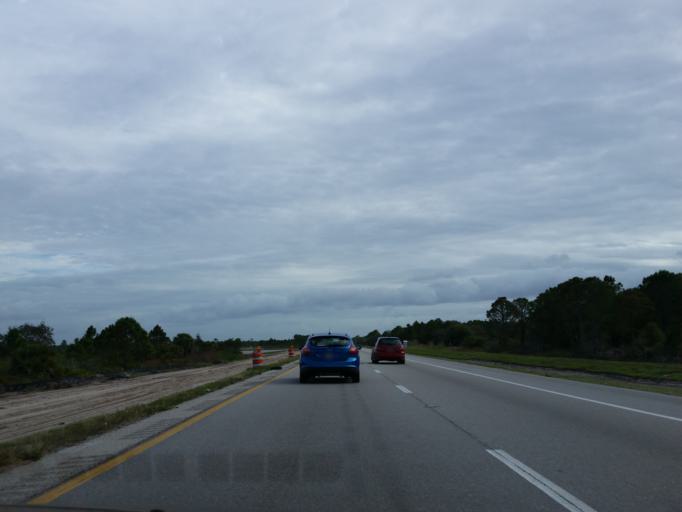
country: US
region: Florida
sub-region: Sarasota County
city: Warm Mineral Springs
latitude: 27.1088
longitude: -82.3094
